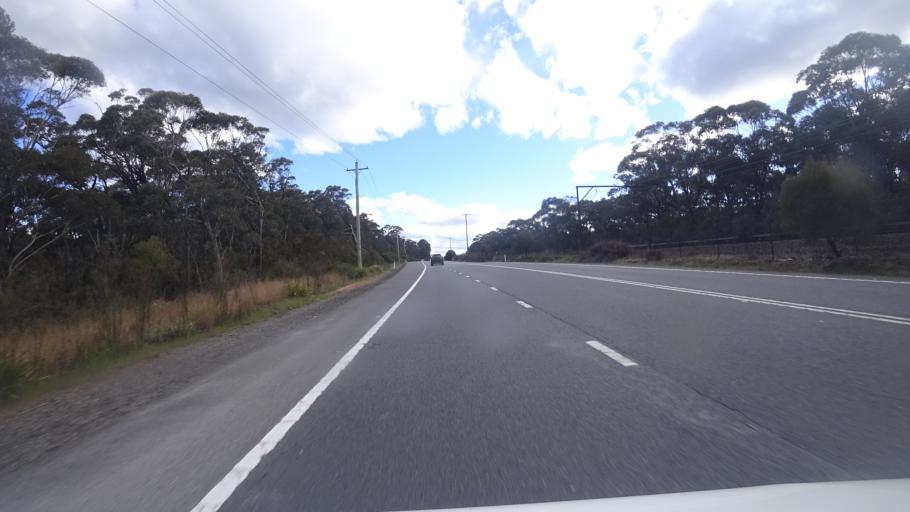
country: AU
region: New South Wales
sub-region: Blue Mountains Municipality
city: Blackheath
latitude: -33.6547
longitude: 150.2815
